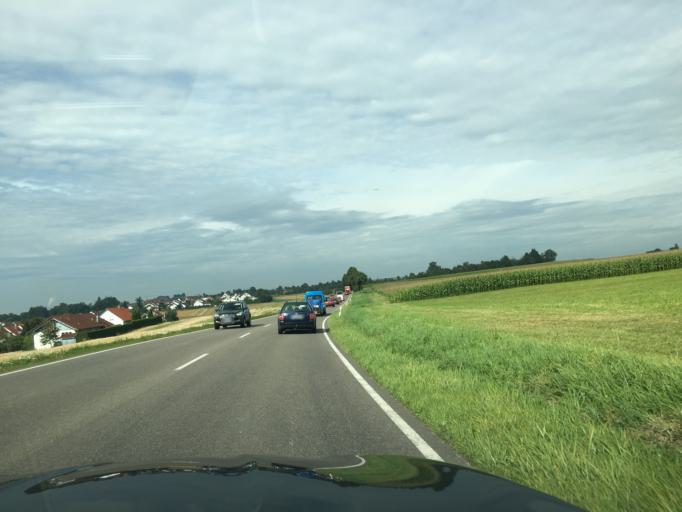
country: DE
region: Baden-Wuerttemberg
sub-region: Tuebingen Region
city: Opfingen
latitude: 48.2893
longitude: 9.7942
